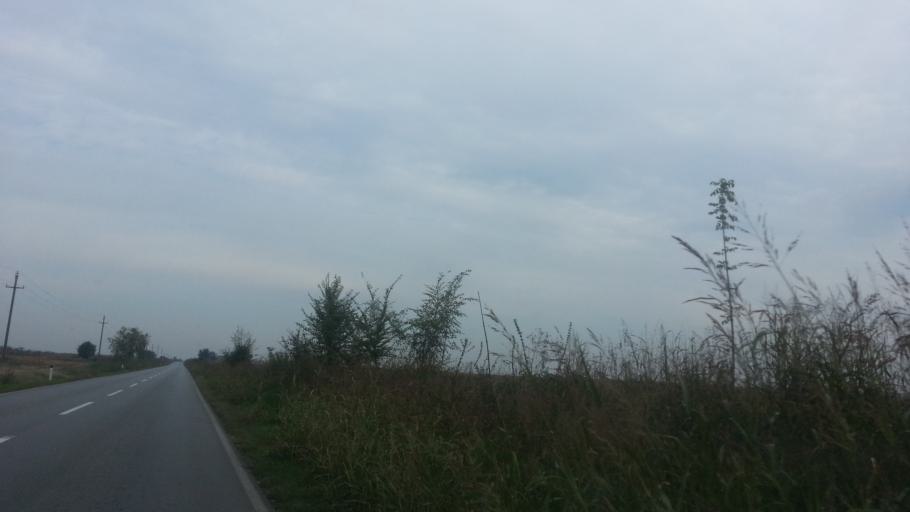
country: RS
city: Belegis
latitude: 45.0337
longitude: 20.3341
